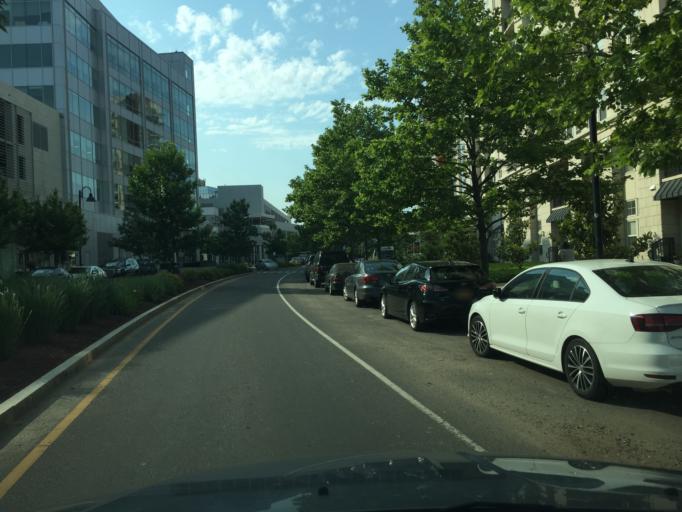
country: US
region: Connecticut
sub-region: Fairfield County
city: Stamford
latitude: 41.0401
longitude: -73.5416
